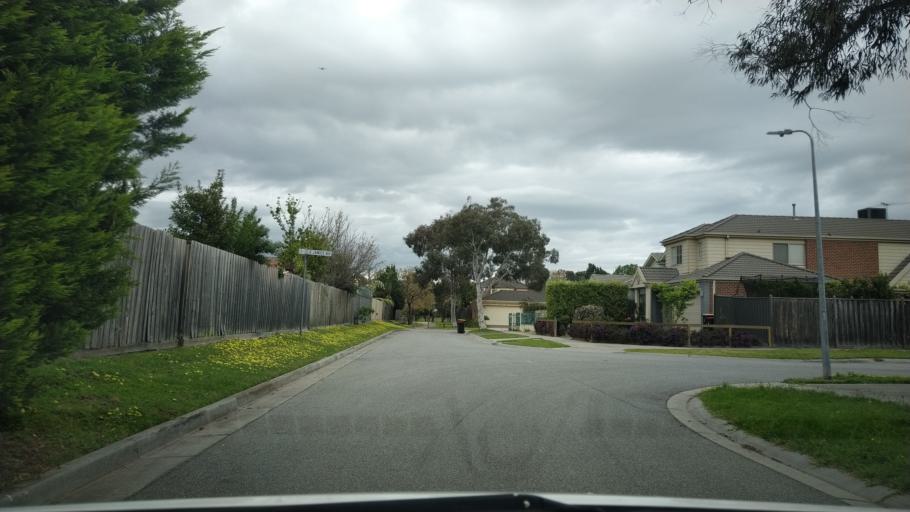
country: AU
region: Victoria
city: Heatherton
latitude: -37.9616
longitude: 145.0774
